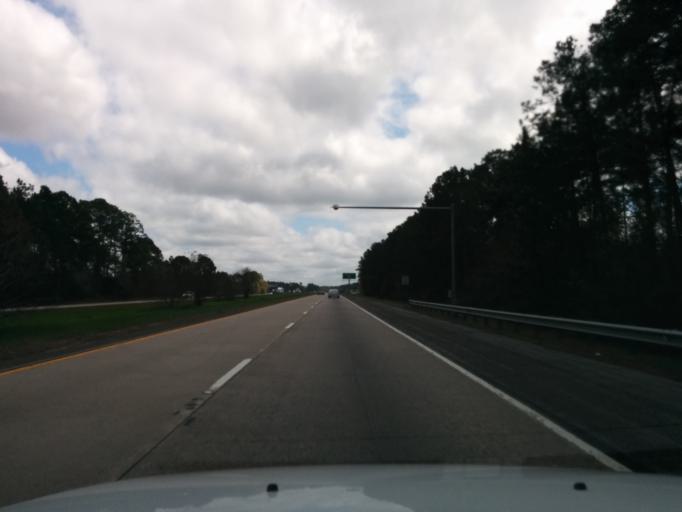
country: US
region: Georgia
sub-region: Chatham County
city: Bloomingdale
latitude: 32.1743
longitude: -81.4513
